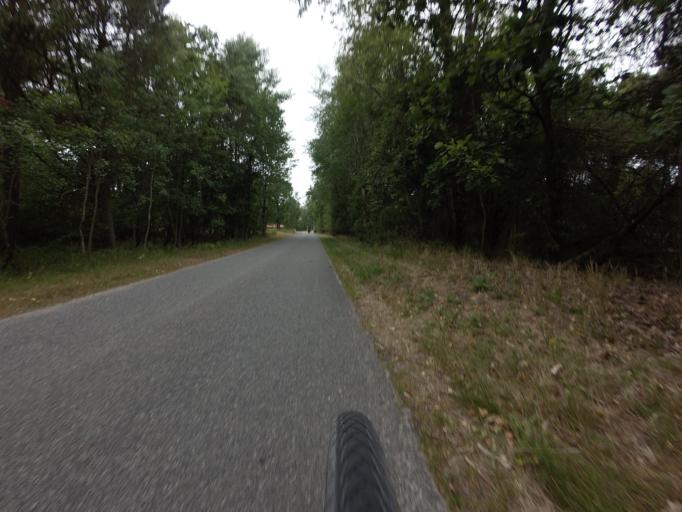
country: DK
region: North Denmark
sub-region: Laeso Kommune
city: Byrum
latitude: 57.2827
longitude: 10.9513
